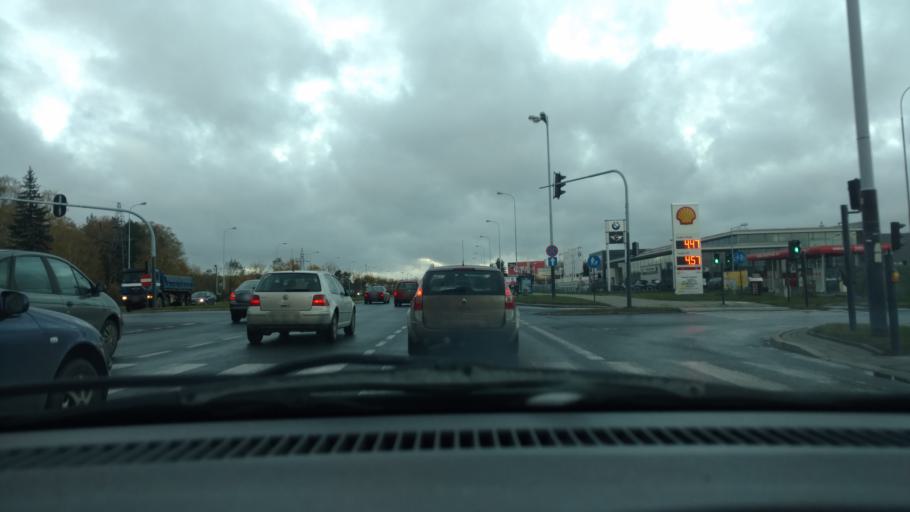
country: PL
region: Lodz Voivodeship
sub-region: Powiat lodzki wschodni
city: Andrespol
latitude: 51.7526
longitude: 19.5828
